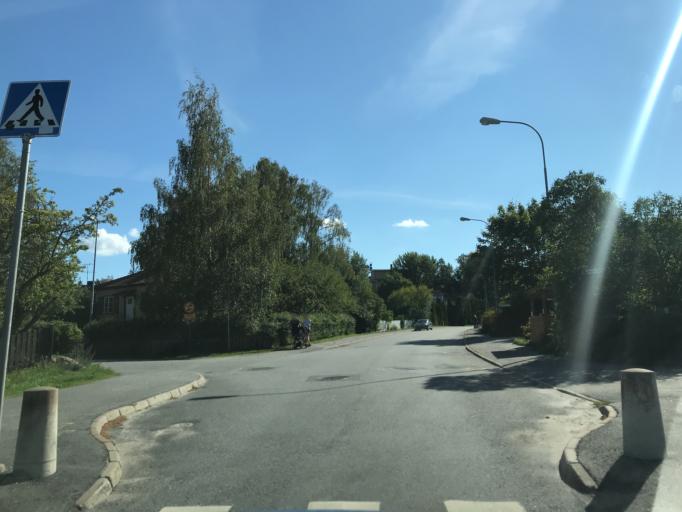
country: SE
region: Stockholm
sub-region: Sollentuna Kommun
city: Sollentuna
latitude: 59.4200
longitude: 17.9504
